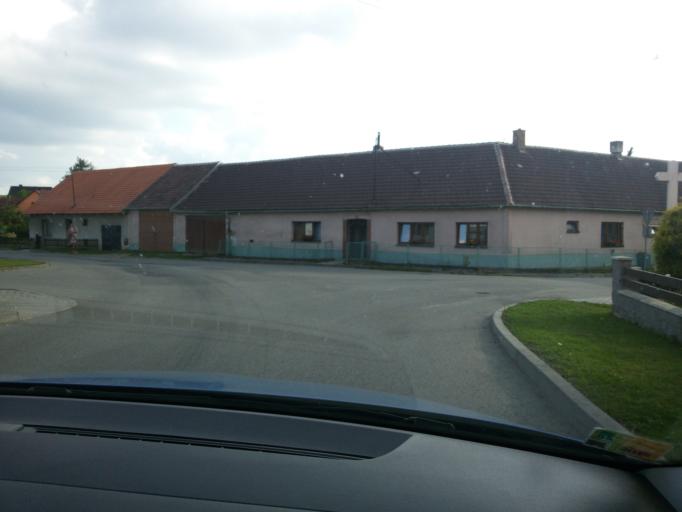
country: CZ
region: South Moravian
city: Olesnice
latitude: 49.4844
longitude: 16.4238
